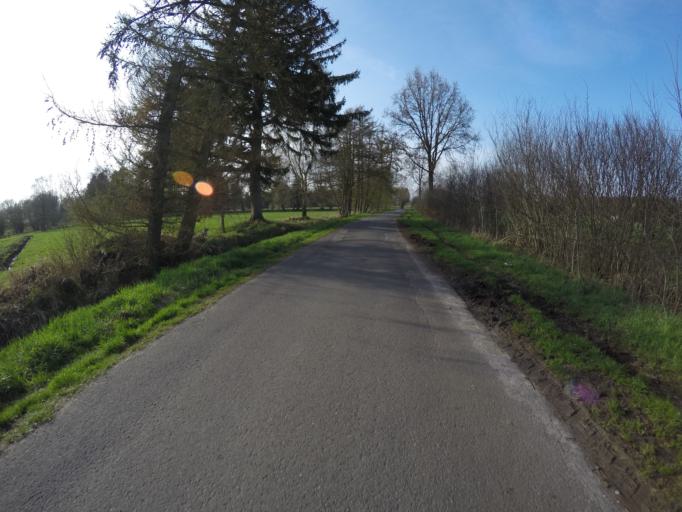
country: DE
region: Schleswig-Holstein
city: Bilsen
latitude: 53.7470
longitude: 9.8739
